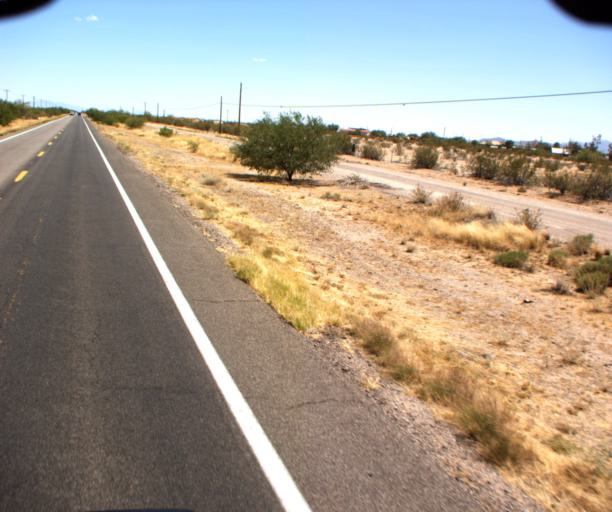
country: US
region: Arizona
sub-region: Pinal County
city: Florence
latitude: 32.9833
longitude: -111.3572
